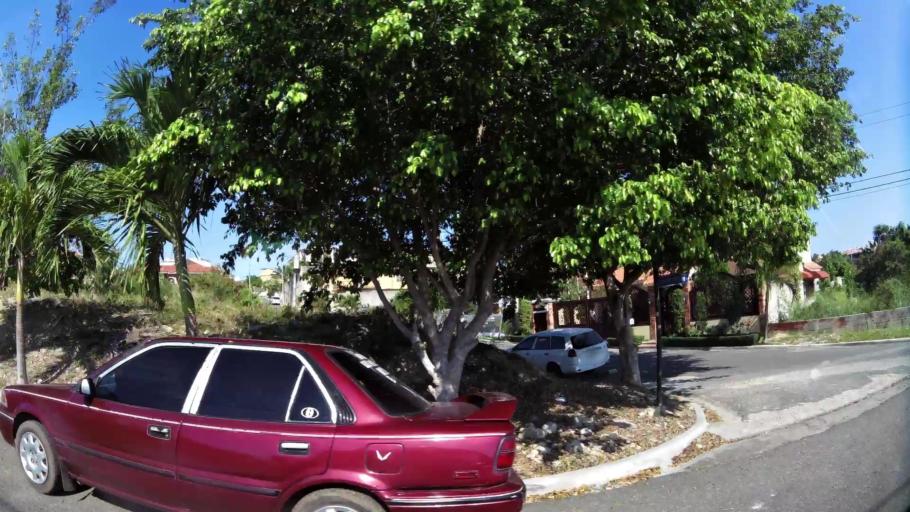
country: DO
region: Nacional
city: Santo Domingo
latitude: 18.4612
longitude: -69.9841
